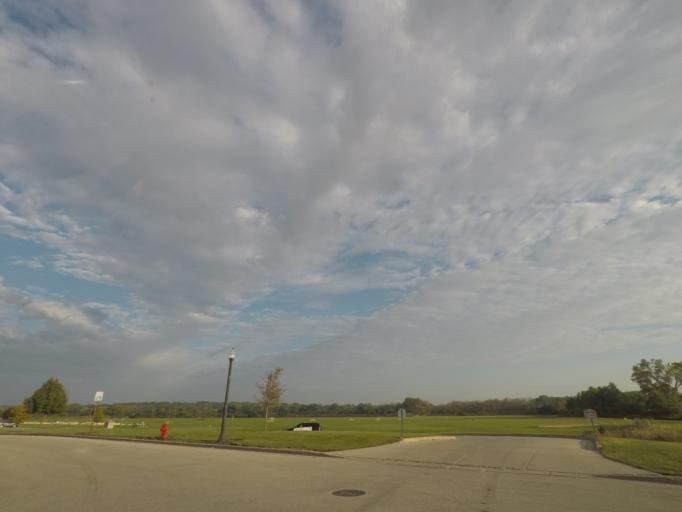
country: US
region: Wisconsin
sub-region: Waukesha County
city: Brookfield
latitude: 43.0389
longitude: -88.1110
